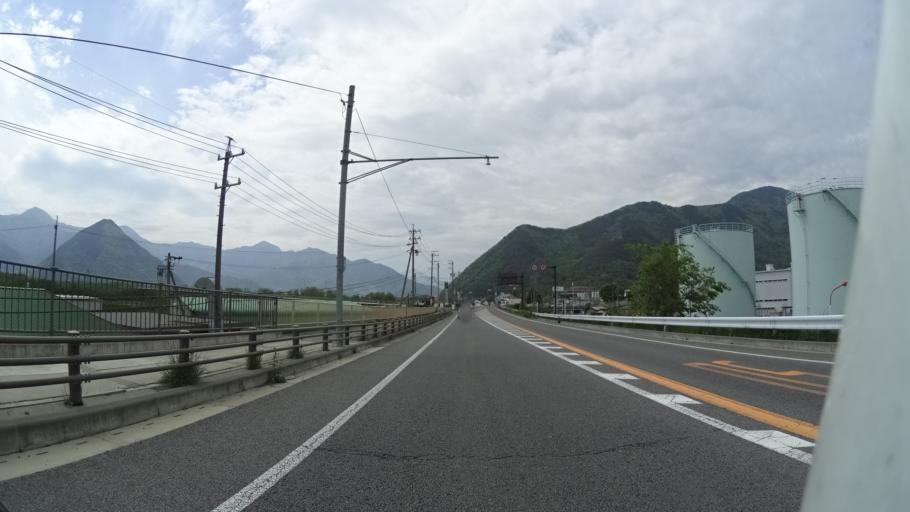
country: JP
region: Nagano
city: Ueda
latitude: 36.4582
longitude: 138.1836
